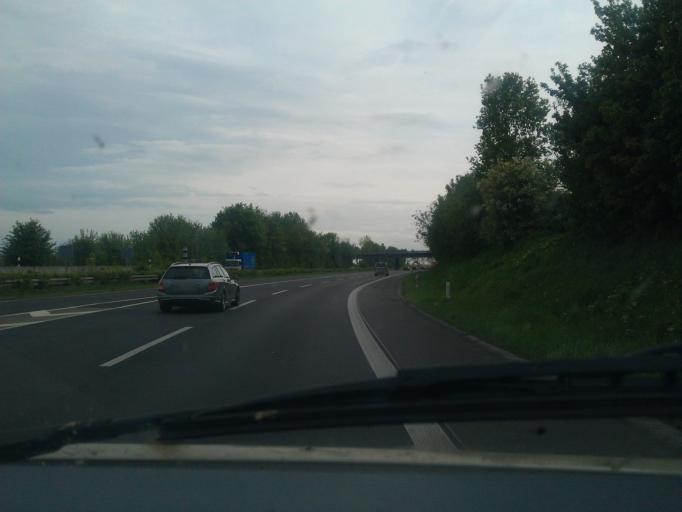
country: DE
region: North Rhine-Westphalia
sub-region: Regierungsbezirk Koln
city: Titz
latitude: 51.0343
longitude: 6.4594
